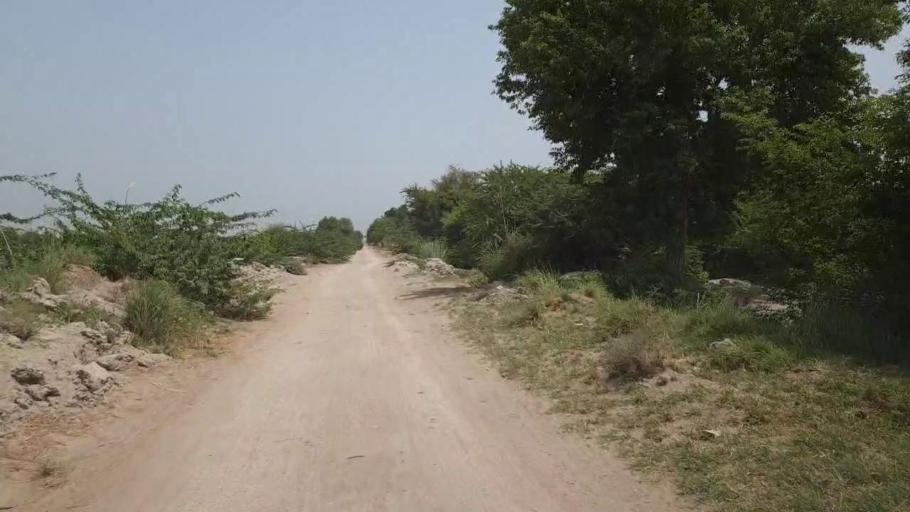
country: PK
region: Sindh
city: Nawabshah
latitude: 26.3112
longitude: 68.3013
